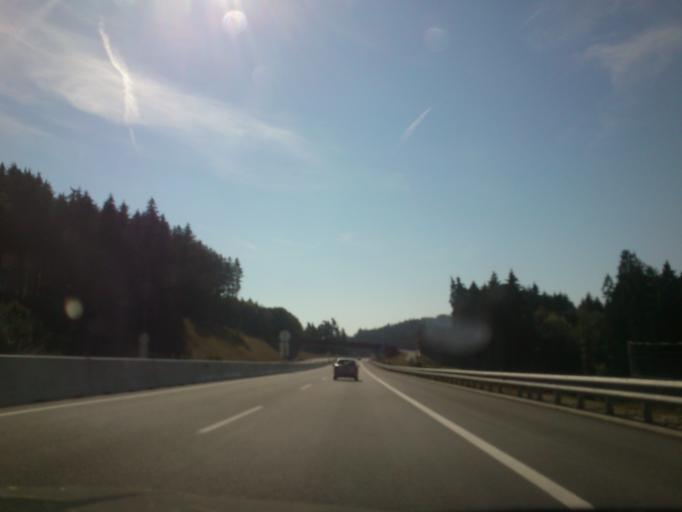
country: AT
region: Upper Austria
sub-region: Politischer Bezirk Freistadt
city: Freistadt
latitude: 48.5230
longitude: 14.5086
